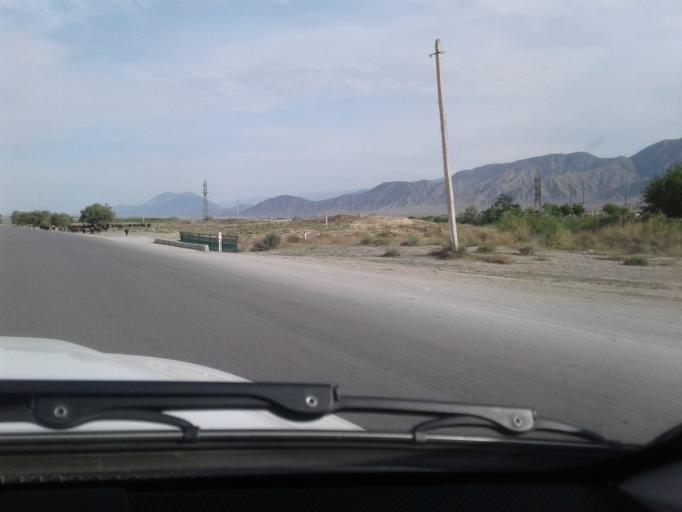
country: TM
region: Ahal
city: Arcabil
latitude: 38.1916
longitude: 57.8419
